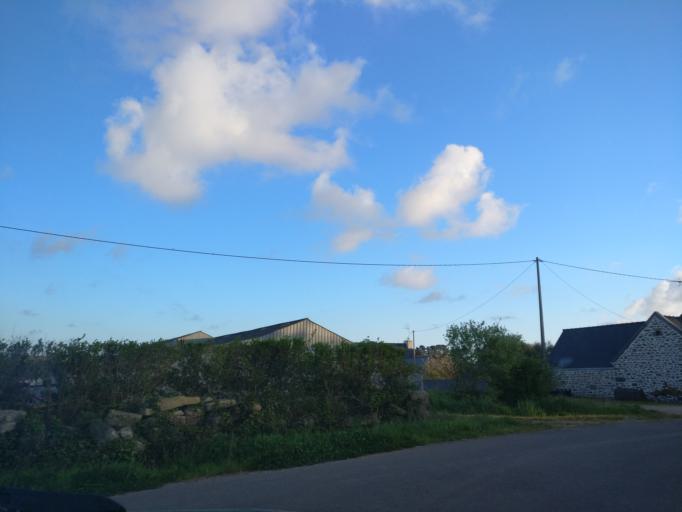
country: FR
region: Brittany
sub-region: Departement du Finistere
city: Lampaul-Plouarzel
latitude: 48.4665
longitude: -4.7453
